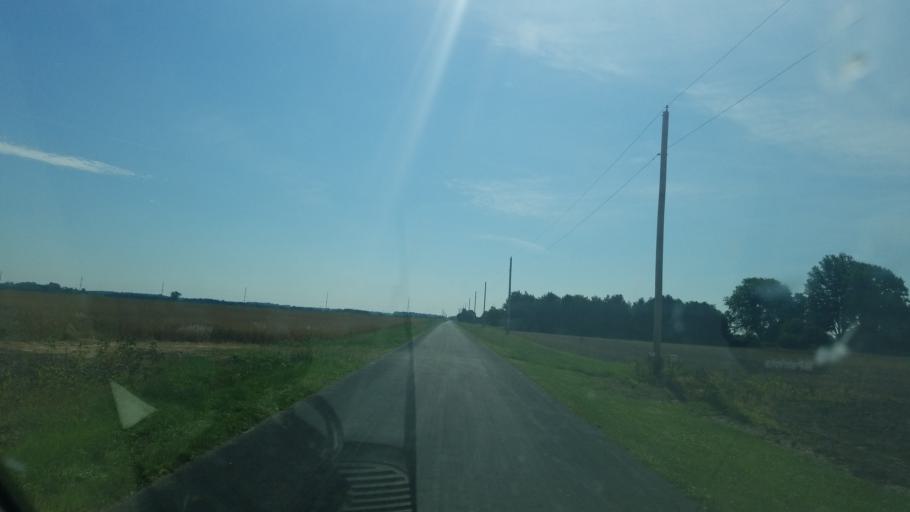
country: US
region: Ohio
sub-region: Wyandot County
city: Carey
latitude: 40.9781
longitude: -83.3125
